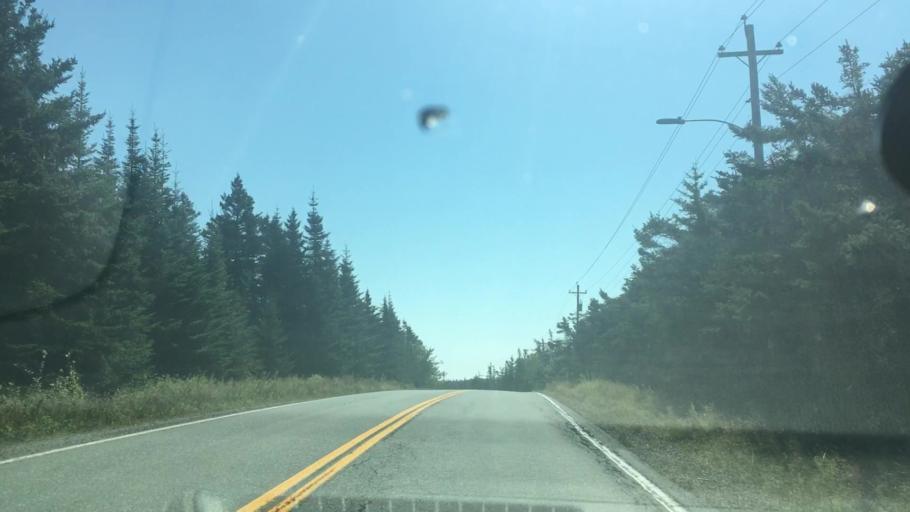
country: CA
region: Nova Scotia
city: New Glasgow
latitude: 44.9200
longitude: -62.3353
